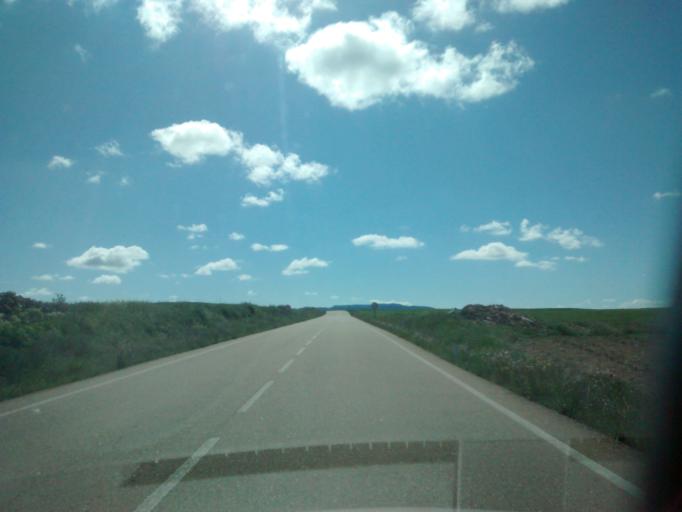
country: ES
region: Aragon
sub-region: Provincia de Zaragoza
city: Perdiguera
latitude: 41.8045
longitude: -0.6882
